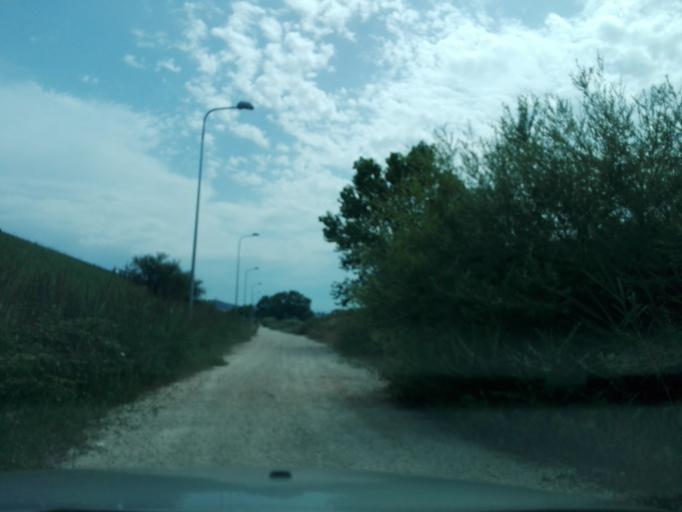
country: IT
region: Abruzzo
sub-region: Provincia di Pescara
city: Cappelle sul Tavo
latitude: 42.4913
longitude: 14.1124
